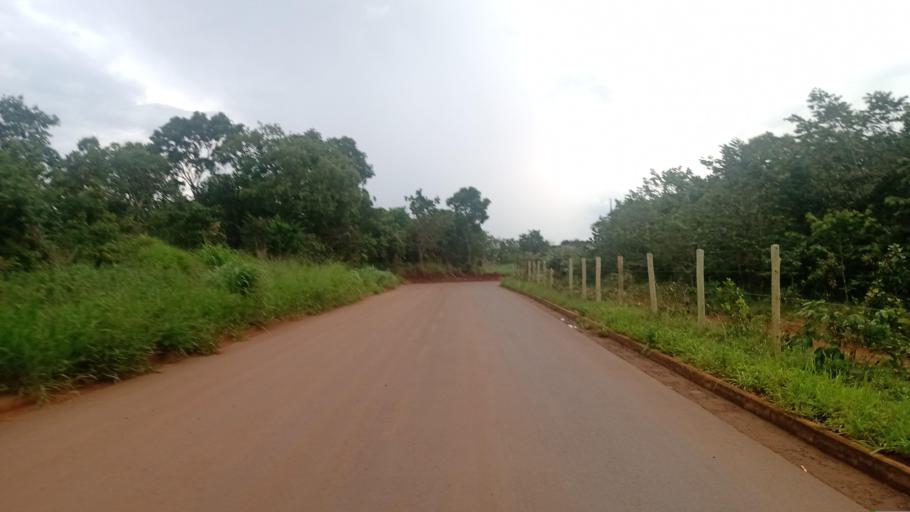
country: BR
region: Goias
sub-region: Senador Canedo
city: Senador Canedo
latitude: -16.7132
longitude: -49.1181
